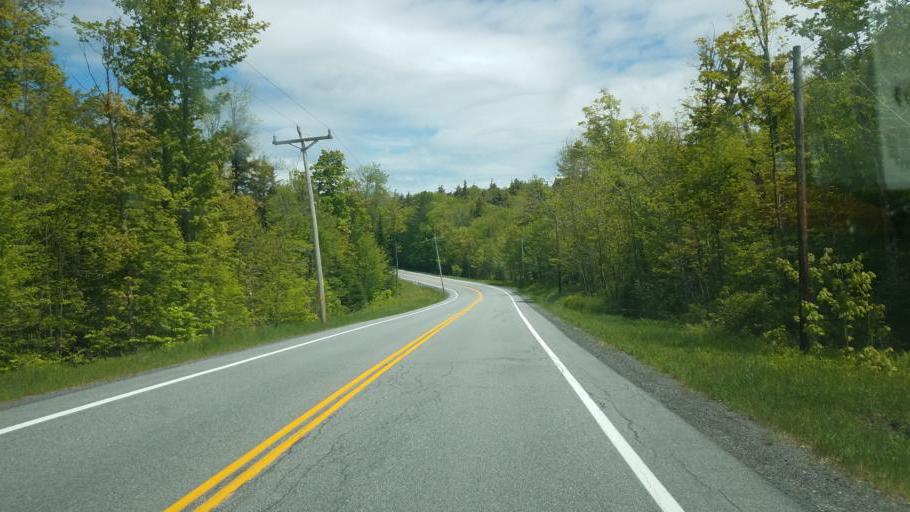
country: US
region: New York
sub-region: Hamilton County
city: Lake Pleasant
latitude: 43.7840
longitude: -74.6927
